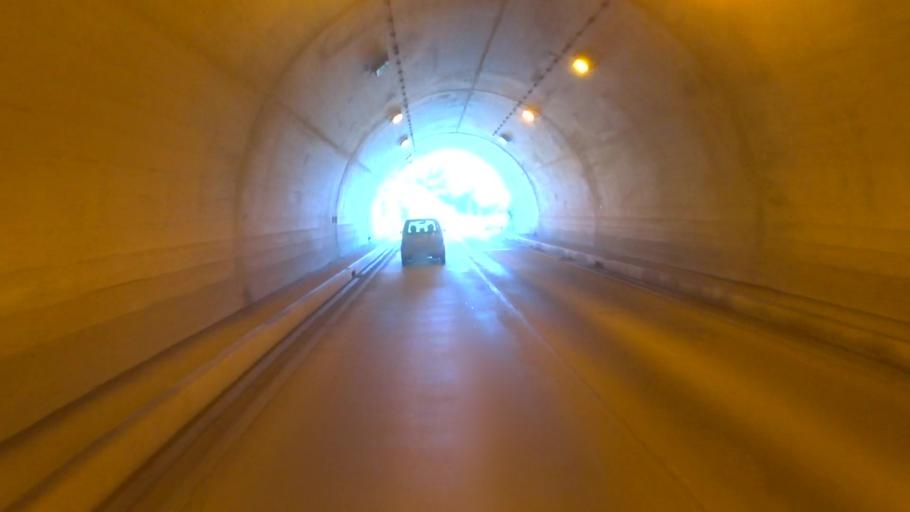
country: JP
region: Kyoto
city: Miyazu
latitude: 35.6773
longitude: 135.2918
